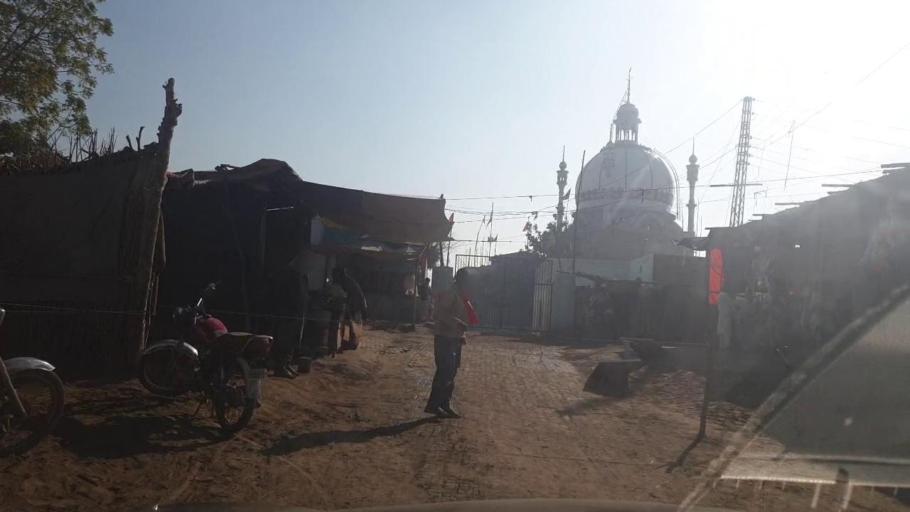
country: PK
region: Sindh
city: Mirpur Mathelo
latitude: 28.0777
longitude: 69.4652
